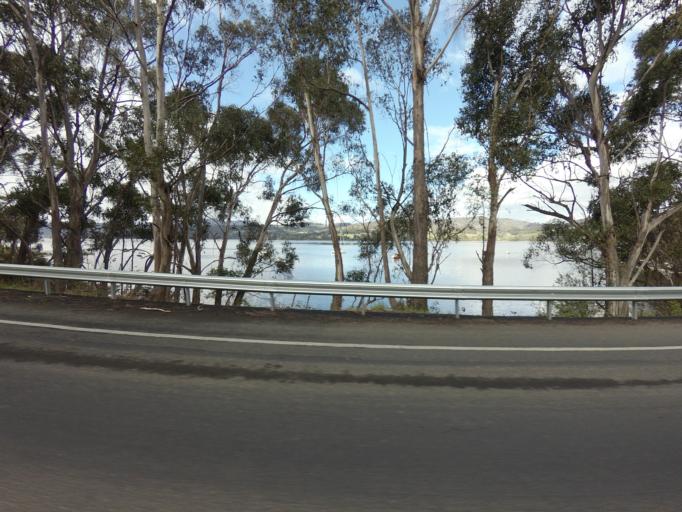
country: AU
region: Tasmania
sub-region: Huon Valley
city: Geeveston
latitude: -43.1478
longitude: 146.9777
